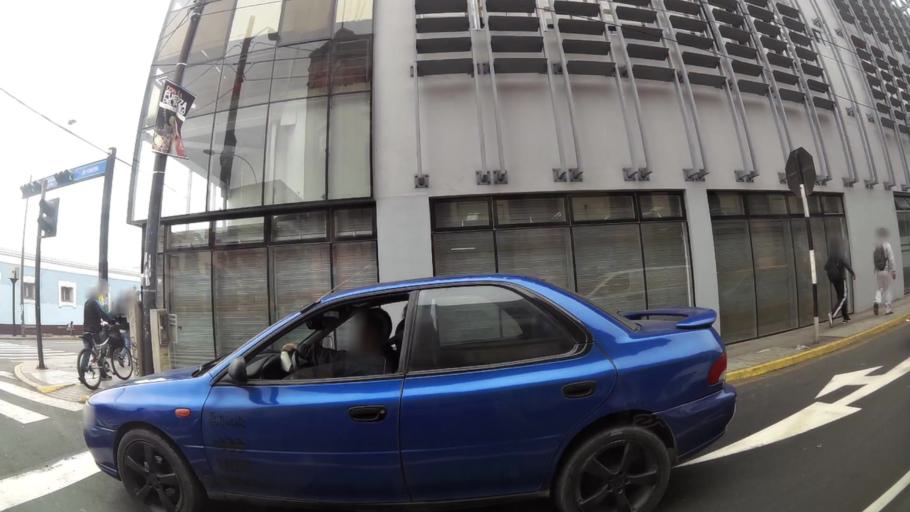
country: PE
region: Lima
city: Lima
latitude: -12.0542
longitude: -77.0406
